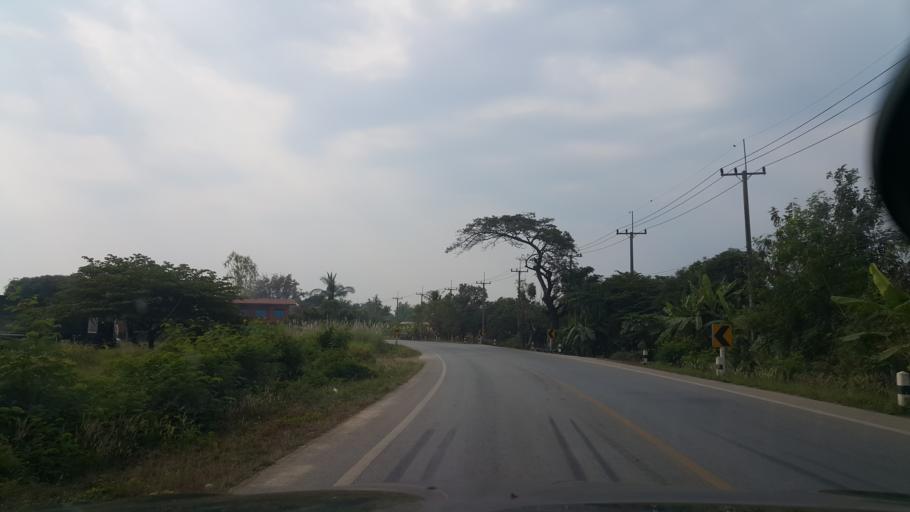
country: TH
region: Sukhothai
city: Si Samrong
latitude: 17.0944
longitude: 99.8838
